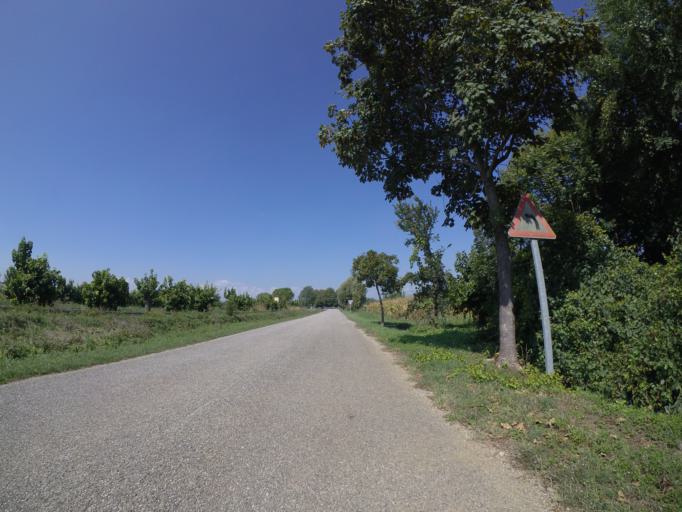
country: IT
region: Friuli Venezia Giulia
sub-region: Provincia di Udine
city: Bertiolo
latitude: 45.9428
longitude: 13.0887
